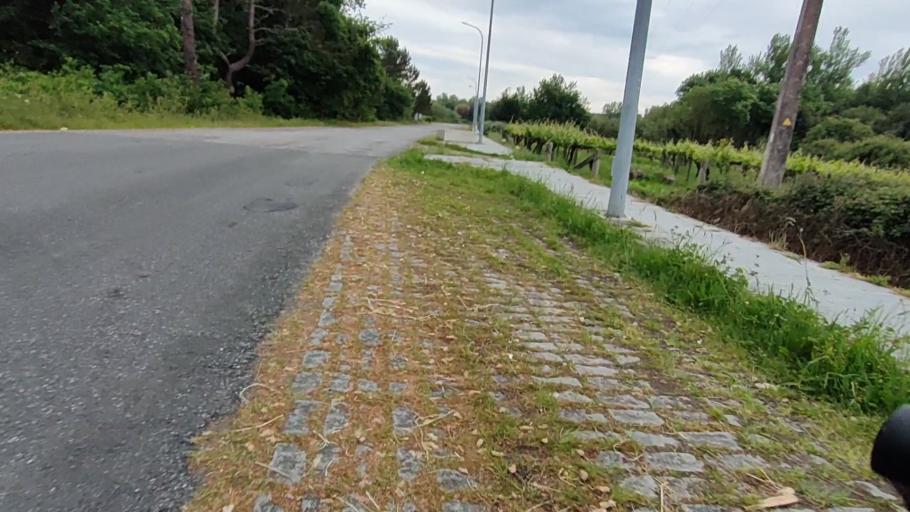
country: ES
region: Galicia
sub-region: Provincia da Coruna
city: Boiro
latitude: 42.6142
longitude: -8.8720
